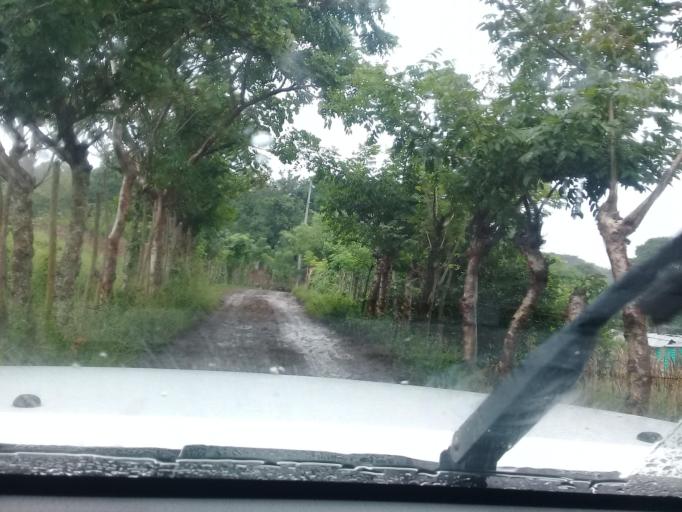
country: MX
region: Veracruz
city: Santiago Tuxtla
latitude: 18.4384
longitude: -95.2951
